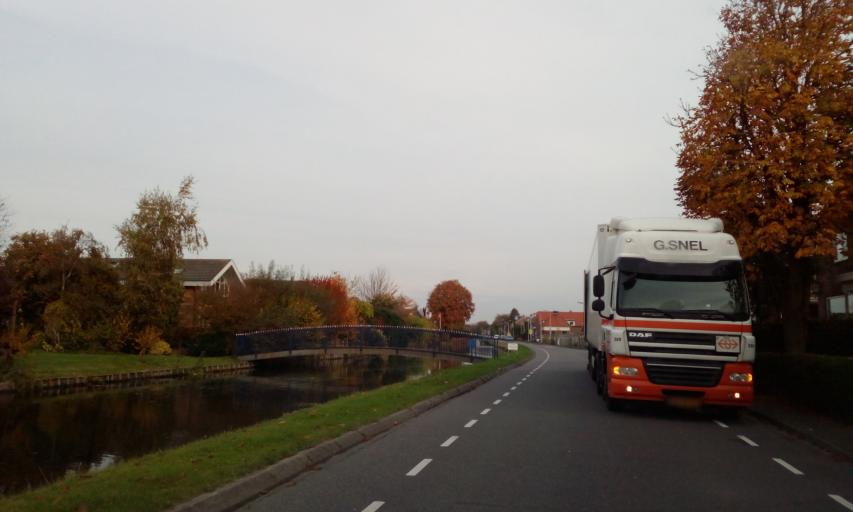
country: NL
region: South Holland
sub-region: Gemeente Lansingerland
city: Berkel en Rodenrijs
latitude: 51.9803
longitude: 4.4655
